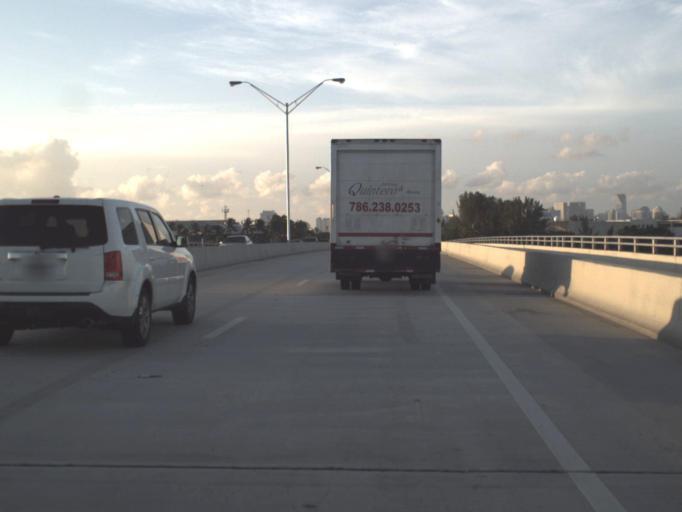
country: US
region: Florida
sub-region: Miami-Dade County
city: Key Biscayne
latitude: 25.7300
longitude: -80.1582
